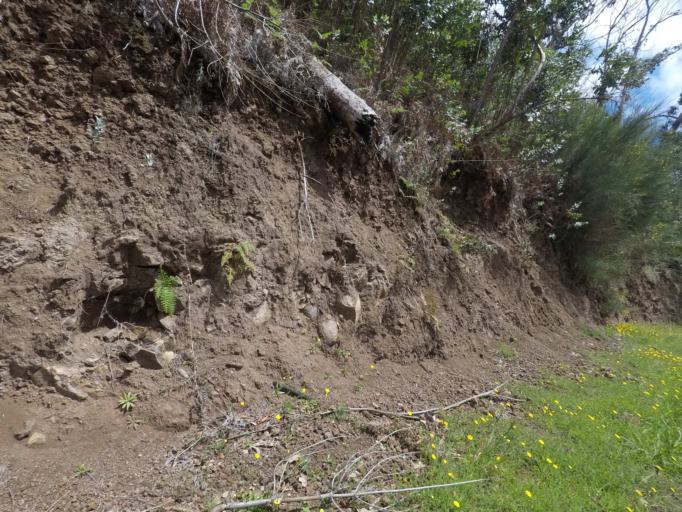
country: PT
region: Madeira
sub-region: Calheta
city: Estreito da Calheta
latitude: 32.7465
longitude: -17.1950
